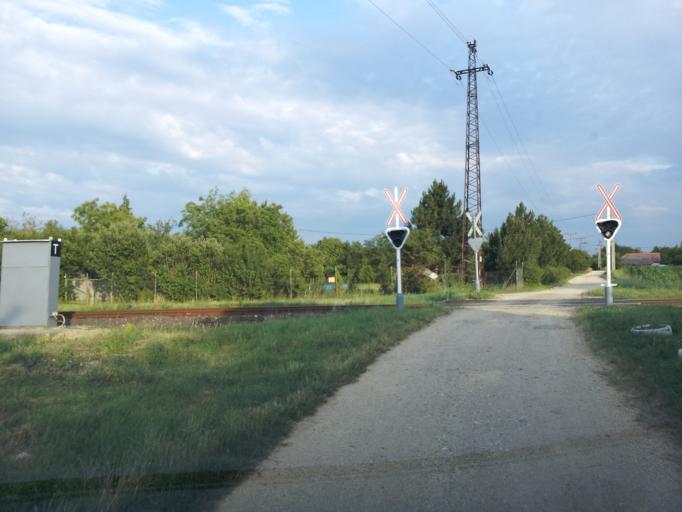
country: HU
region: Veszprem
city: Balatonkenese
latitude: 47.0214
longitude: 18.1759
